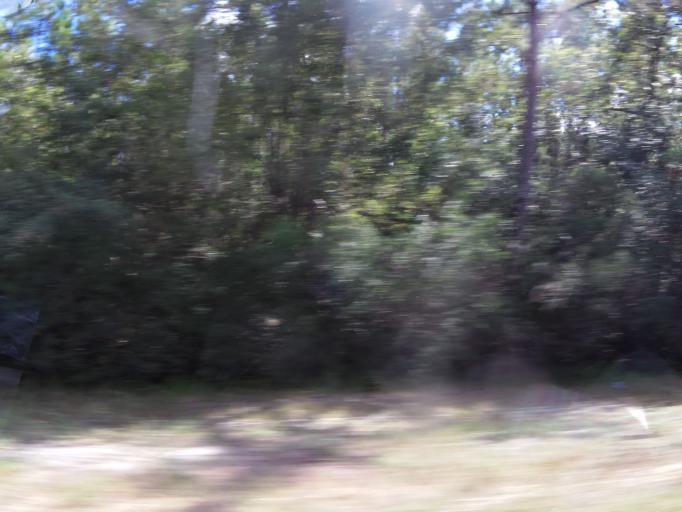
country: US
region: Florida
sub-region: Hamilton County
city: Jasper
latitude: 30.5989
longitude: -82.6674
